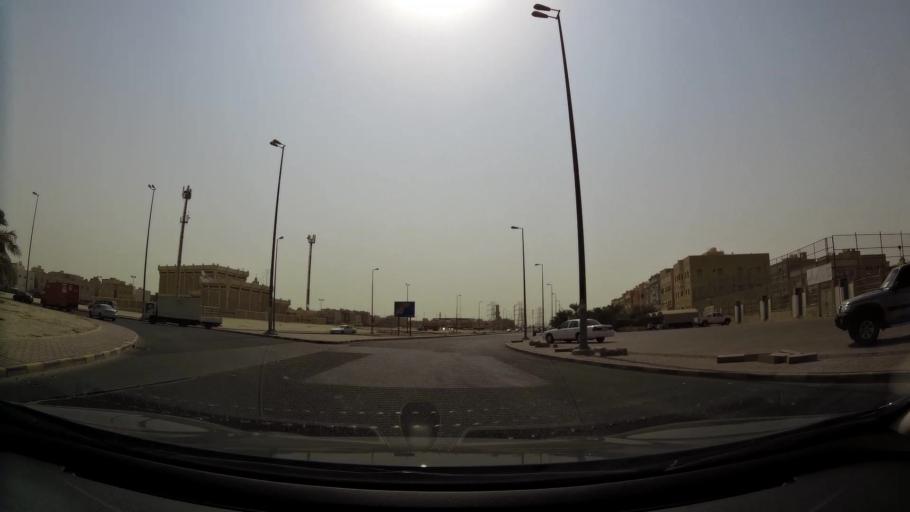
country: KW
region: Muhafazat al Jahra'
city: Al Jahra'
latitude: 29.3058
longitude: 47.7240
